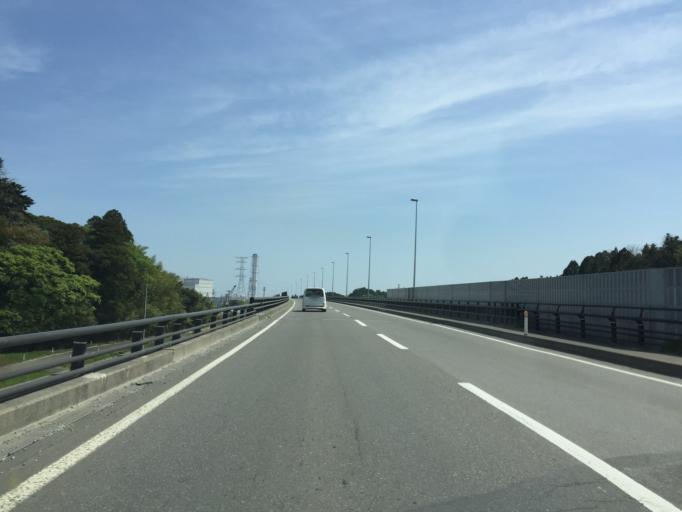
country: JP
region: Miyagi
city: Marumori
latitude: 37.8519
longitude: 140.9244
